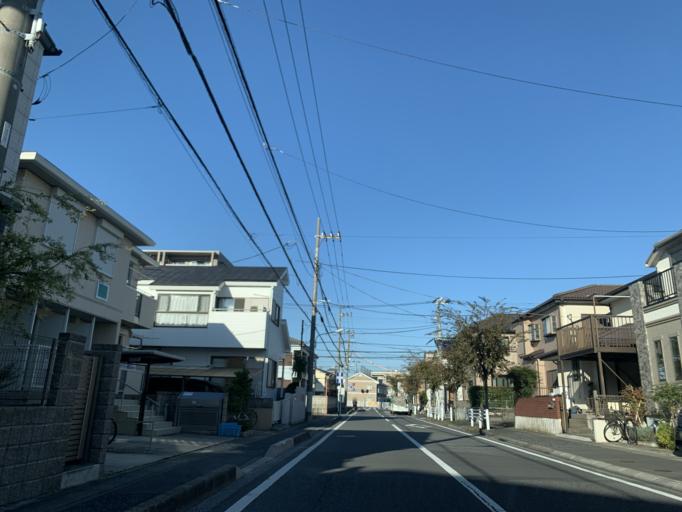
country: JP
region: Tokyo
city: Urayasu
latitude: 35.6531
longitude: 139.8900
